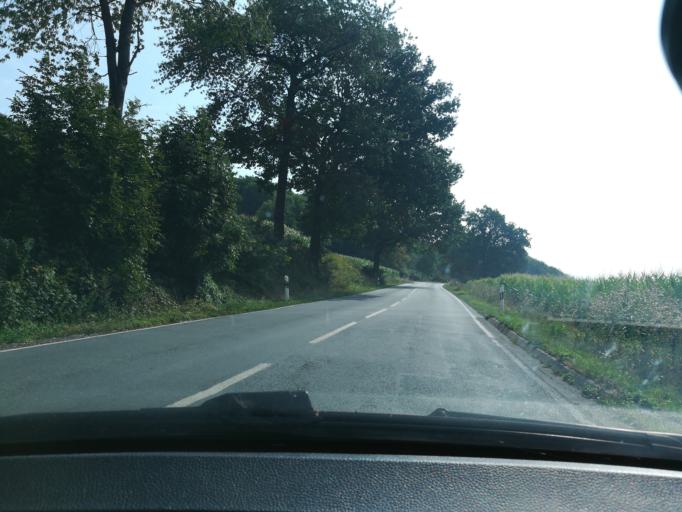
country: DE
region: North Rhine-Westphalia
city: Borgholzhausen
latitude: 52.1127
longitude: 8.3151
